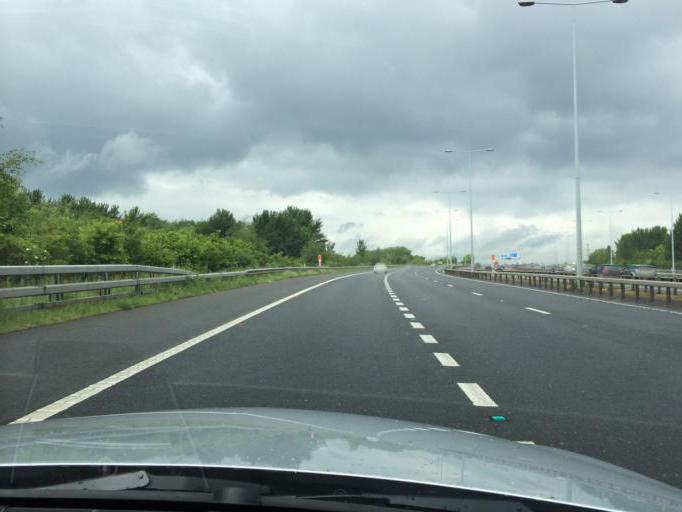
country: GB
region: England
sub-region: Trafford
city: Sale
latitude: 53.4311
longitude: -2.3034
